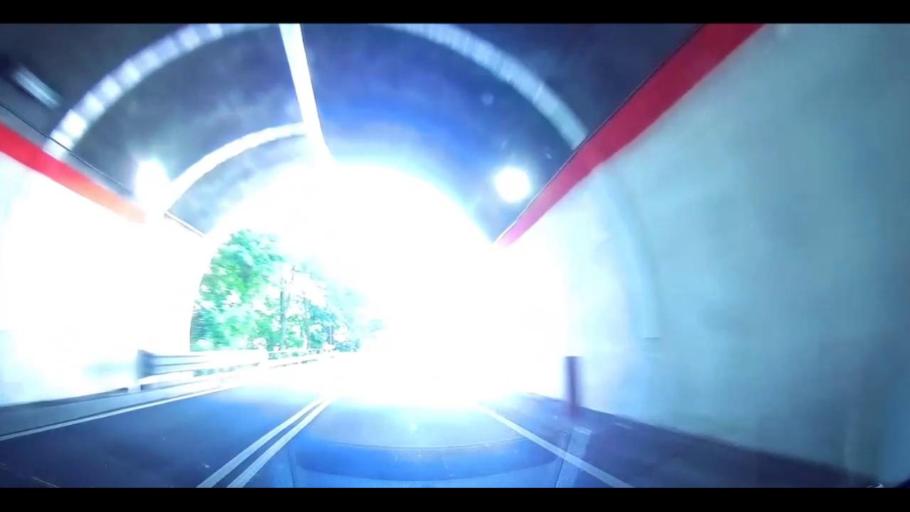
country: IT
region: Calabria
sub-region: Provincia di Cosenza
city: Celico
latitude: 39.3048
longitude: 16.3542
